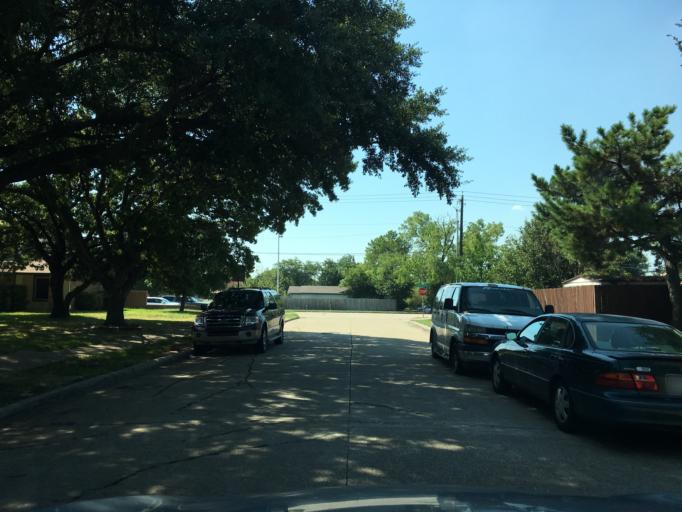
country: US
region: Texas
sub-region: Dallas County
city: Garland
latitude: 32.9313
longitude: -96.6528
